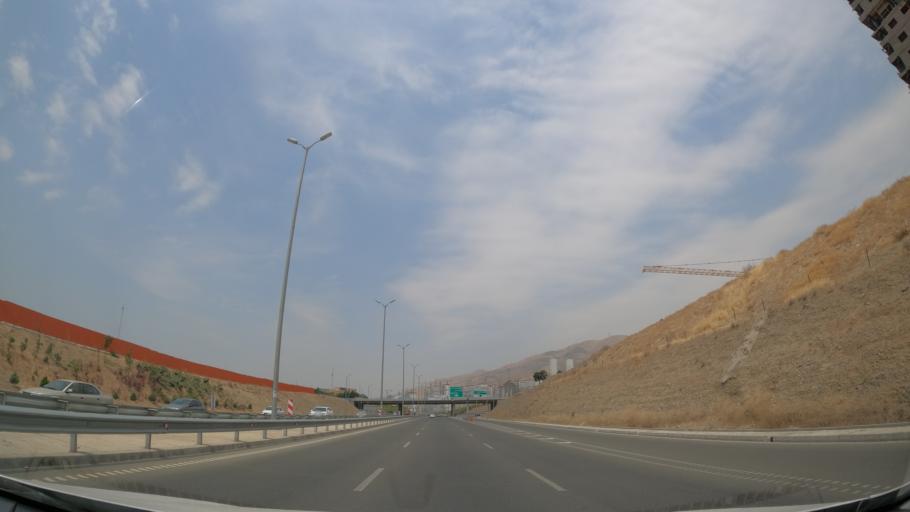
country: IR
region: Tehran
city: Shahr-e Qods
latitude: 35.7489
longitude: 51.1759
